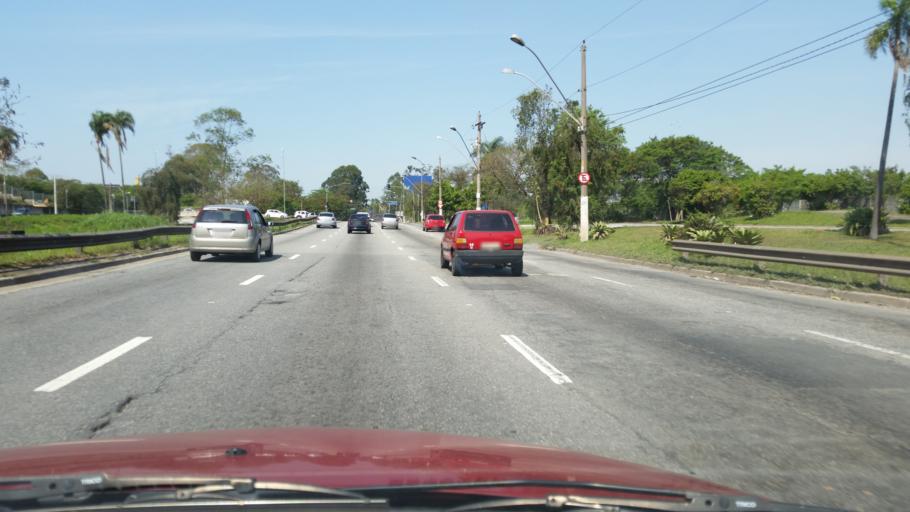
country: BR
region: Sao Paulo
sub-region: Santo Andre
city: Santo Andre
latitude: -23.6558
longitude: -46.5032
